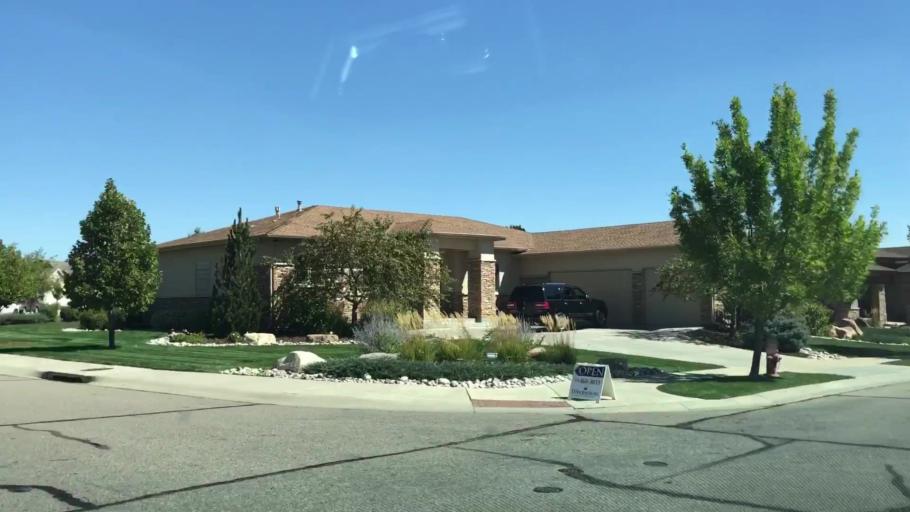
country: US
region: Colorado
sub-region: Weld County
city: Johnstown
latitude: 40.3989
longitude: -104.9812
